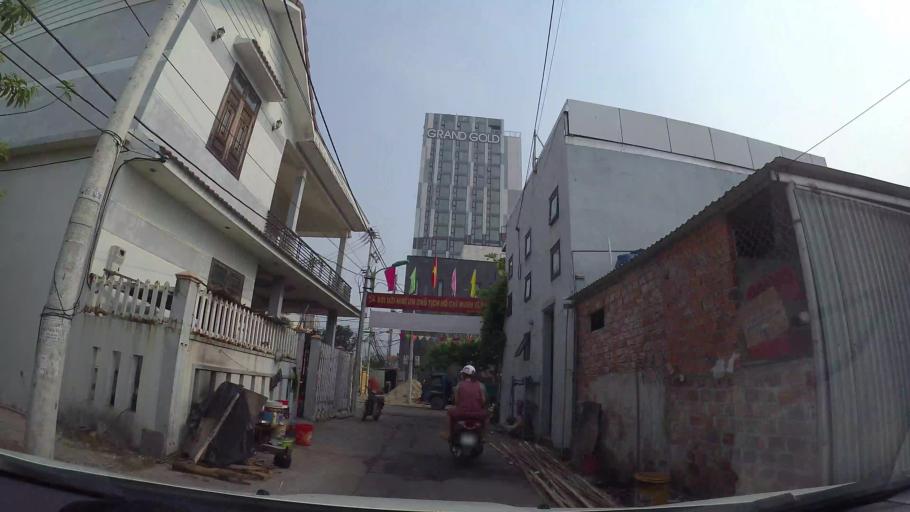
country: VN
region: Da Nang
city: Son Tra
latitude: 16.0930
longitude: 108.2510
